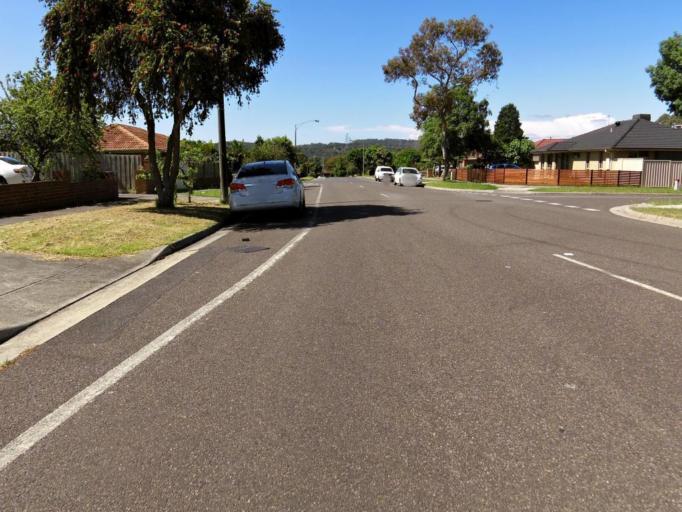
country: AU
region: Victoria
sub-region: Casey
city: Endeavour Hills
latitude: -37.9689
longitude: 145.2449
